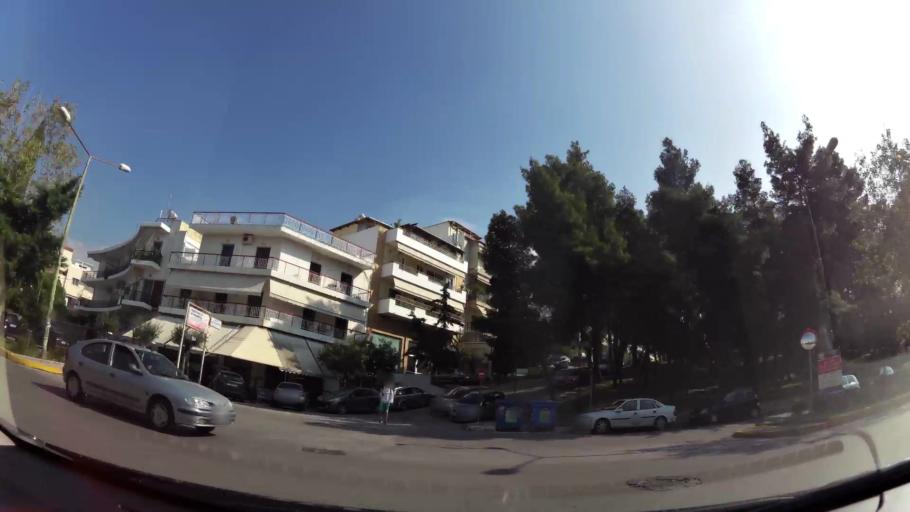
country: GR
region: Attica
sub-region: Nomarchia Athinas
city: Agios Dimitrios
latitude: 37.9326
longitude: 23.7484
